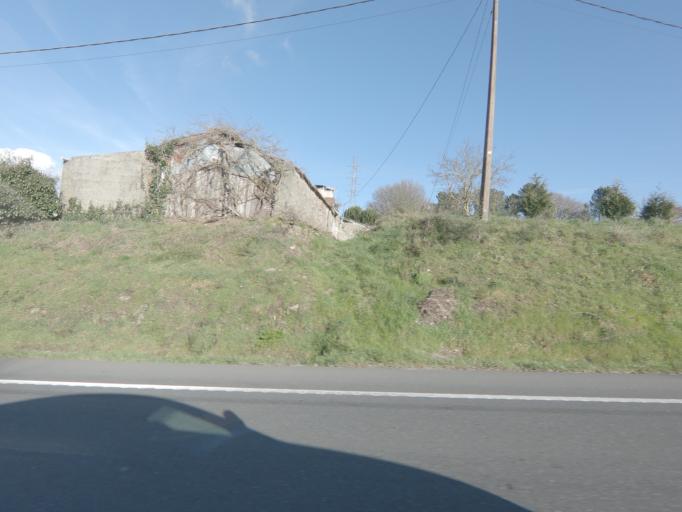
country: ES
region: Galicia
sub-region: Provincia de Pontevedra
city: Silleda
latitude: 42.7140
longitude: -8.2799
